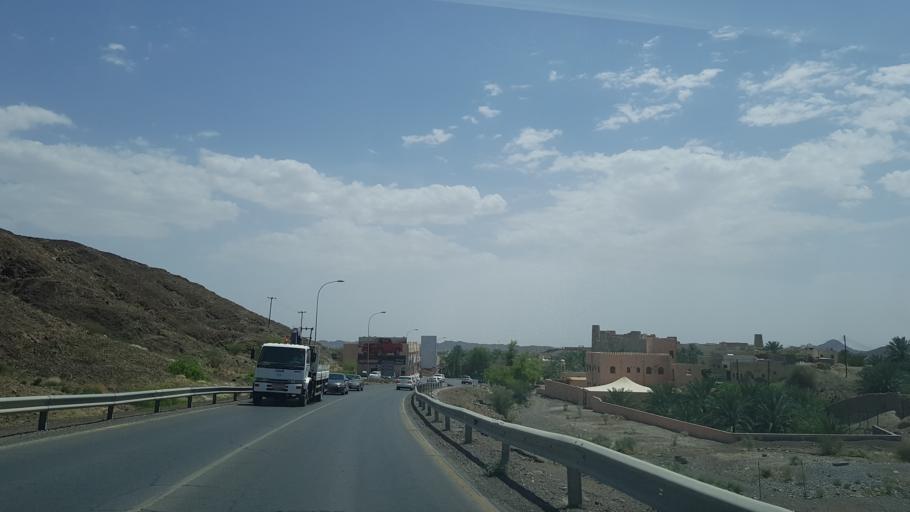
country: OM
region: Muhafazat ad Dakhiliyah
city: Bahla'
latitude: 22.9694
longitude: 57.3022
